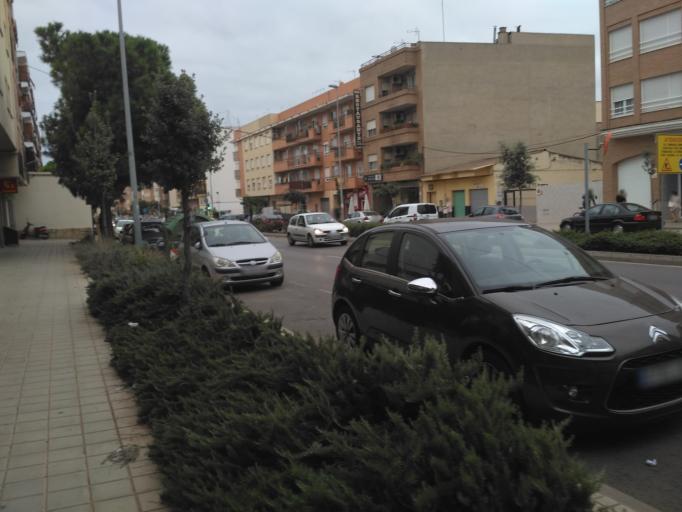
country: ES
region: Valencia
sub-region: Provincia de Castello
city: Castello de la Plana
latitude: 39.9871
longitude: -0.0595
